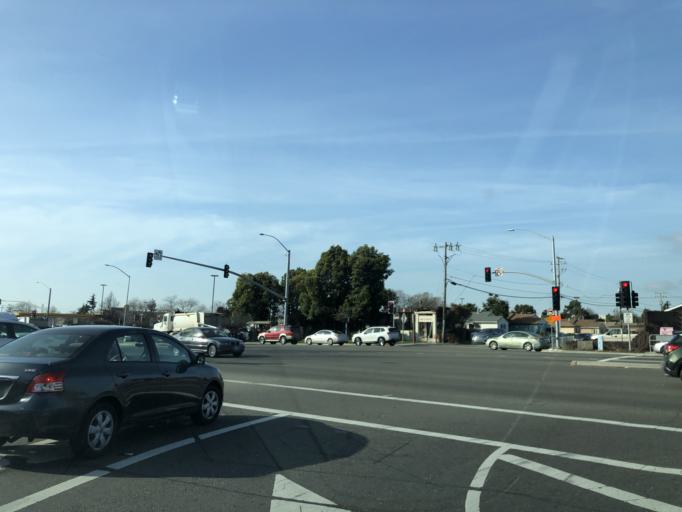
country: US
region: California
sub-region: Alameda County
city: San Leandro
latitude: 37.7181
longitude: -122.1793
